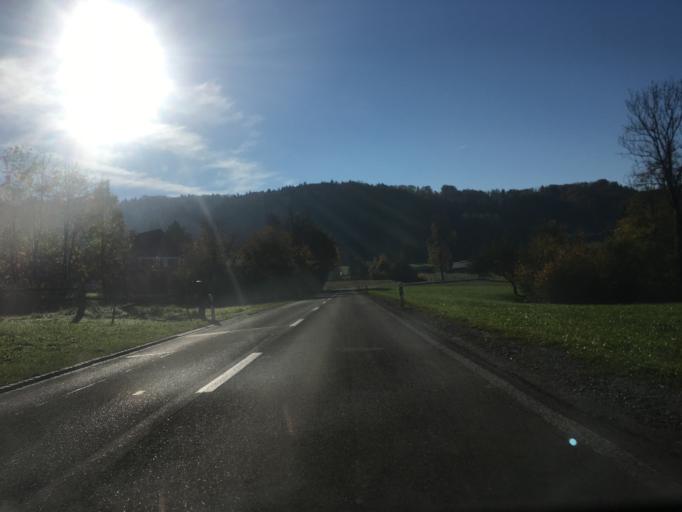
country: CH
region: Zurich
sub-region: Bezirk Affoltern
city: Schachen
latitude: 47.3140
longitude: 8.4926
